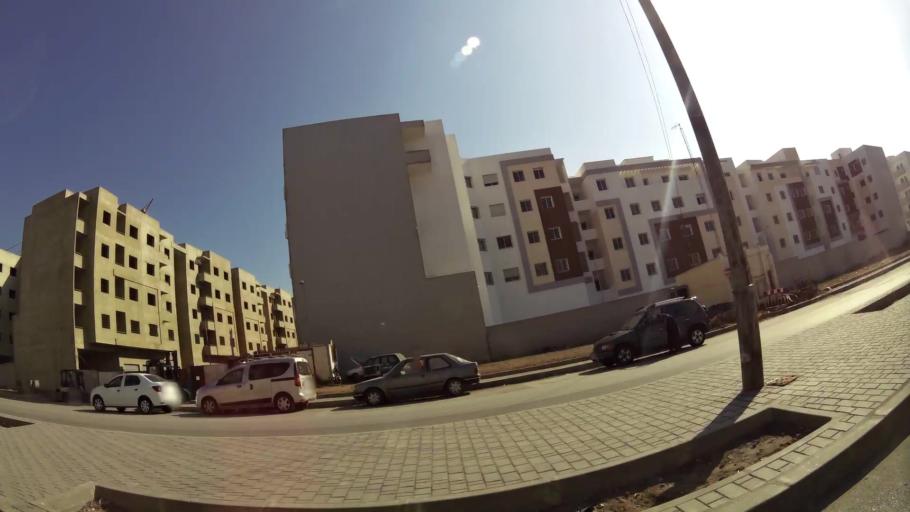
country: MA
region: Rabat-Sale-Zemmour-Zaer
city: Sale
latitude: 34.0569
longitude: -6.7975
